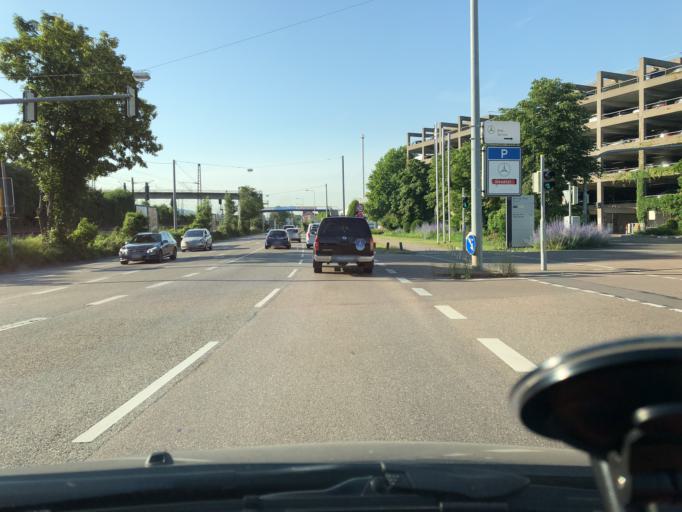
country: DE
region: Baden-Wuerttemberg
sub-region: Regierungsbezirk Stuttgart
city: Stuttgart-Ost
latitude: 48.7877
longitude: 9.2438
